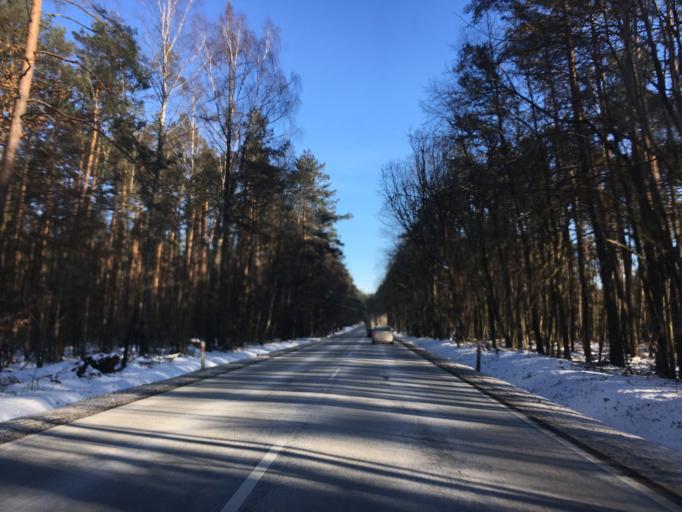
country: PL
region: Pomeranian Voivodeship
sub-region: Powiat koscierski
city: Koscierzyna
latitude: 54.1126
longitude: 17.9130
